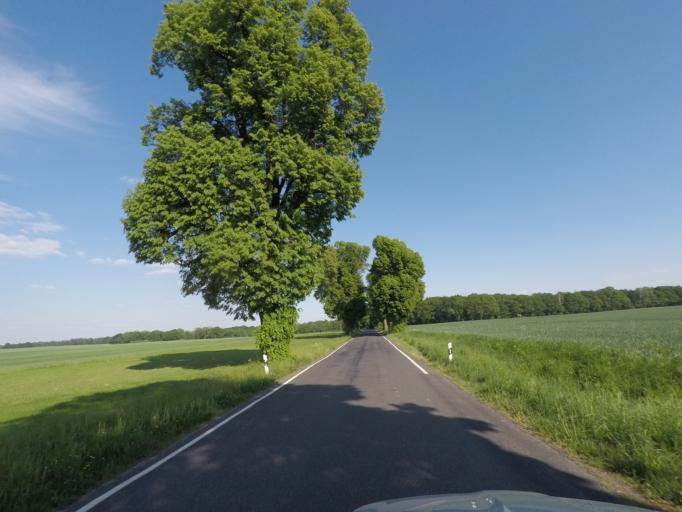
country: DE
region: Brandenburg
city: Hohenfinow
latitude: 52.7252
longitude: 13.8812
